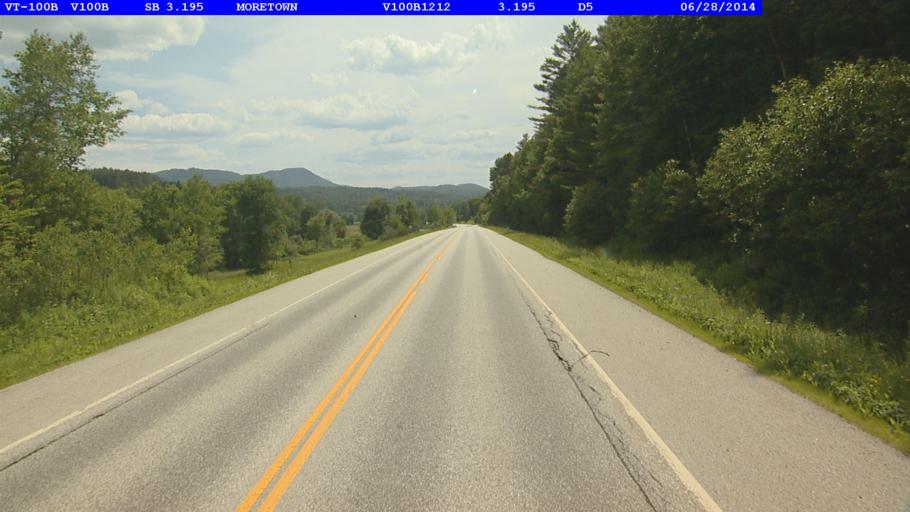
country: US
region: Vermont
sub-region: Washington County
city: Waterbury
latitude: 44.2752
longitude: -72.7444
